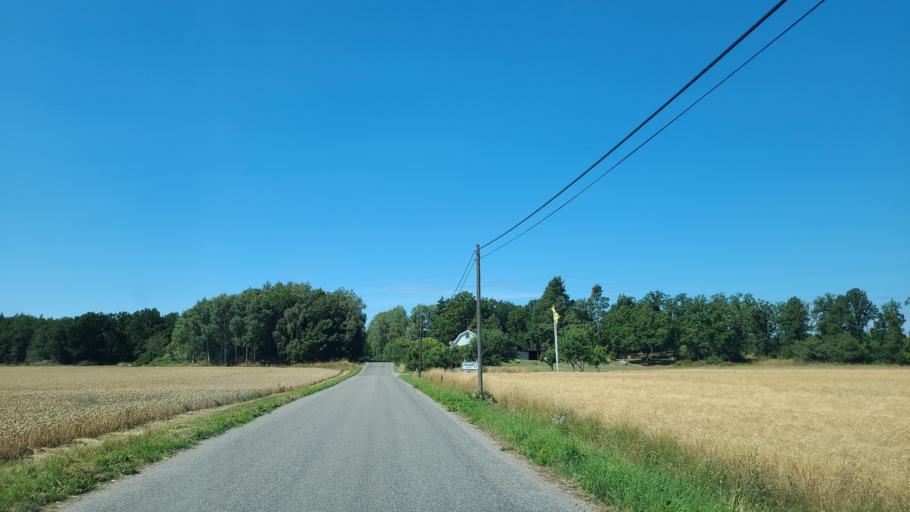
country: SE
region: Kalmar
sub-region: Kalmar Kommun
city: Ljungbyholm
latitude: 56.5758
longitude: 16.0889
